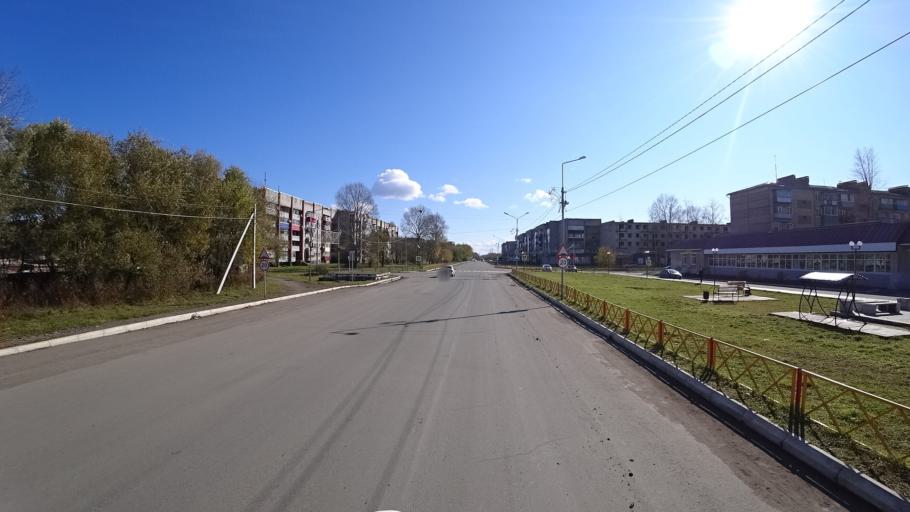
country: RU
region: Khabarovsk Krai
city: Amursk
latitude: 50.1005
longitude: 136.5121
